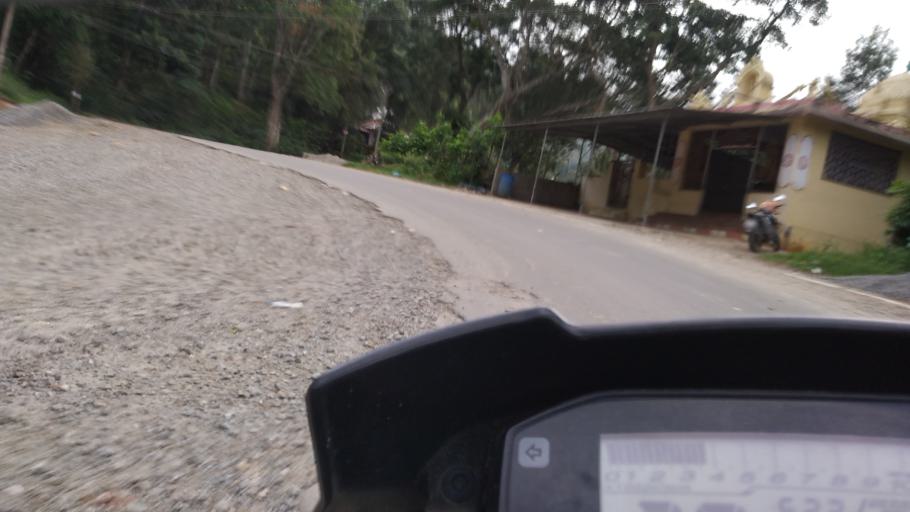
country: IN
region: Tamil Nadu
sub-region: Theni
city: Bodinayakkanur
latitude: 10.0121
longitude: 77.2374
